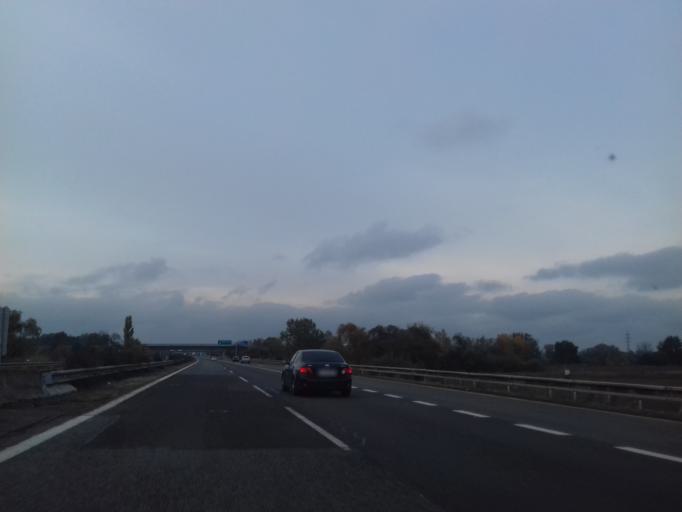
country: CZ
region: South Moravian
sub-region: Okres Breclav
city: Lanzhot
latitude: 48.6361
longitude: 17.0036
